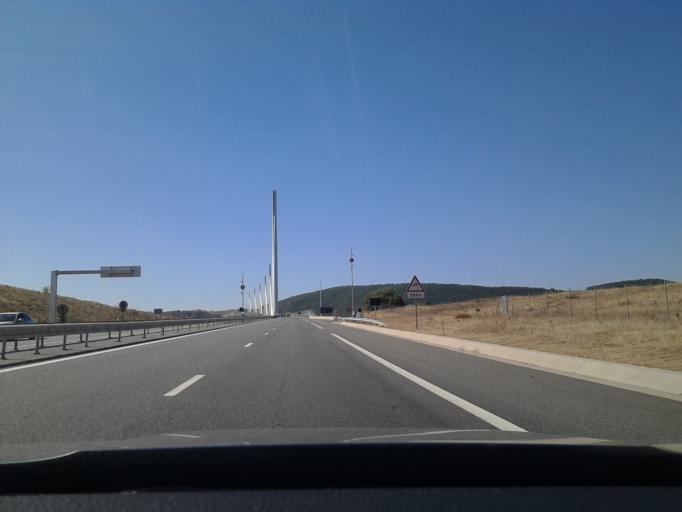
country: FR
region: Midi-Pyrenees
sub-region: Departement de l'Aveyron
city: Creissels
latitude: 44.0934
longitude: 3.0210
